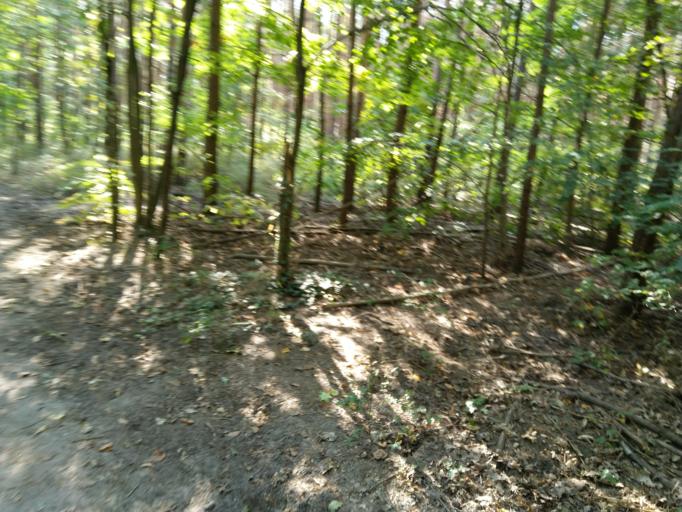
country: DE
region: Brandenburg
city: Woltersdorf
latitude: 52.4427
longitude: 13.7507
